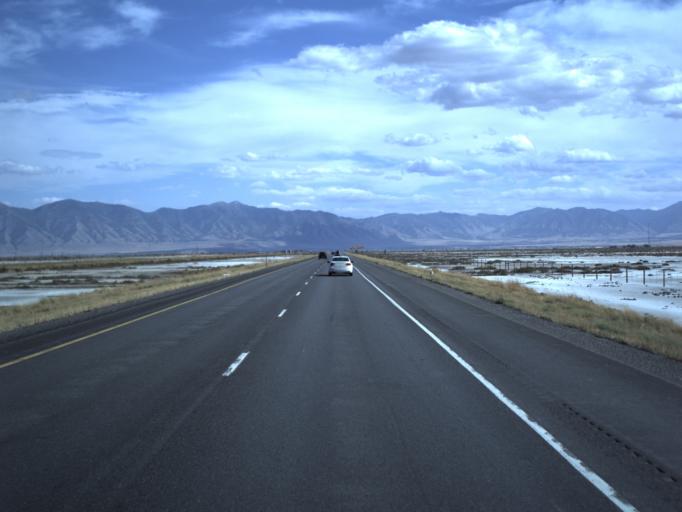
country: US
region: Utah
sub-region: Tooele County
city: Grantsville
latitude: 40.6985
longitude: -112.4833
